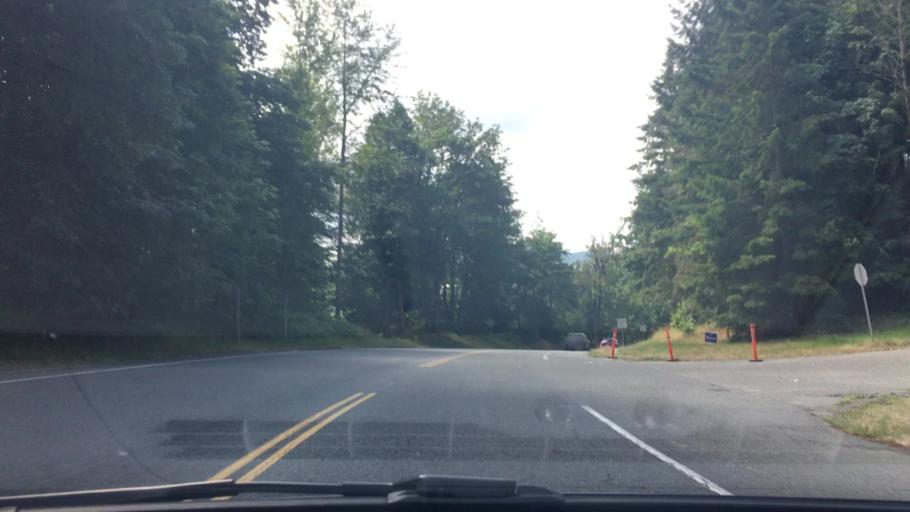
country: US
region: Washington
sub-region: King County
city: City of Sammamish
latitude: 47.5690
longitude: -122.0359
